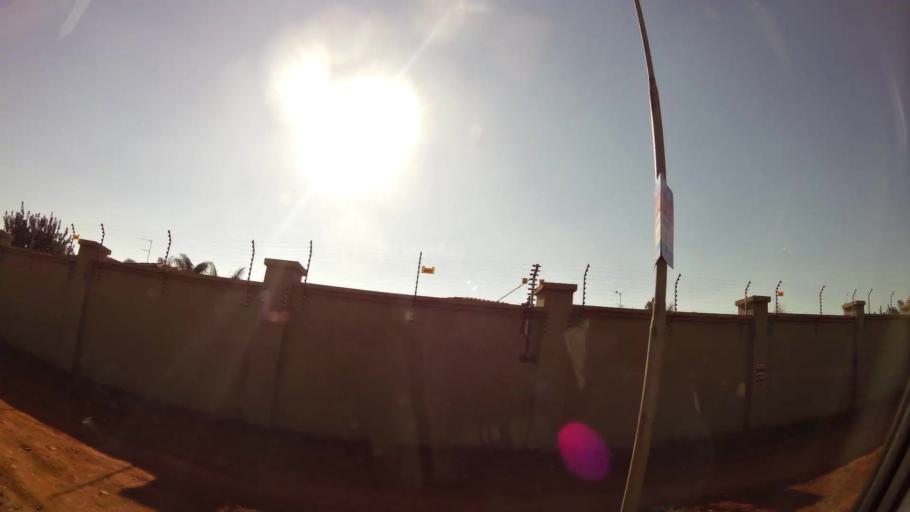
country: ZA
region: Gauteng
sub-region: City of Tshwane Metropolitan Municipality
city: Centurion
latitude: -25.8400
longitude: 28.2819
